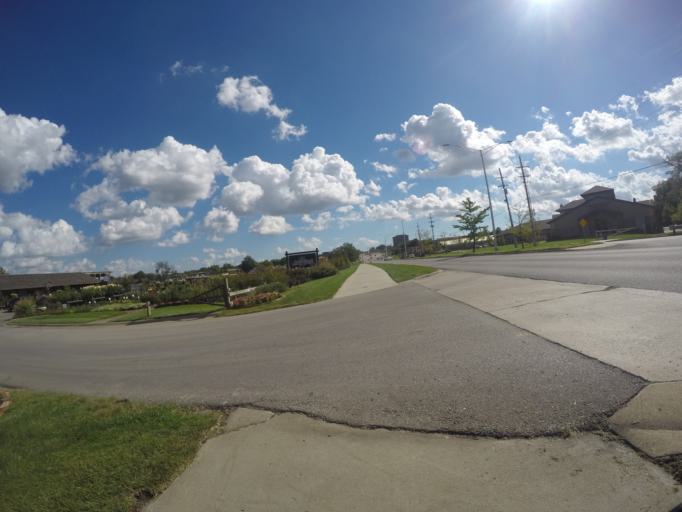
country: US
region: Kansas
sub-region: Johnson County
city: Leawood
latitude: 38.9377
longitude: -94.6395
